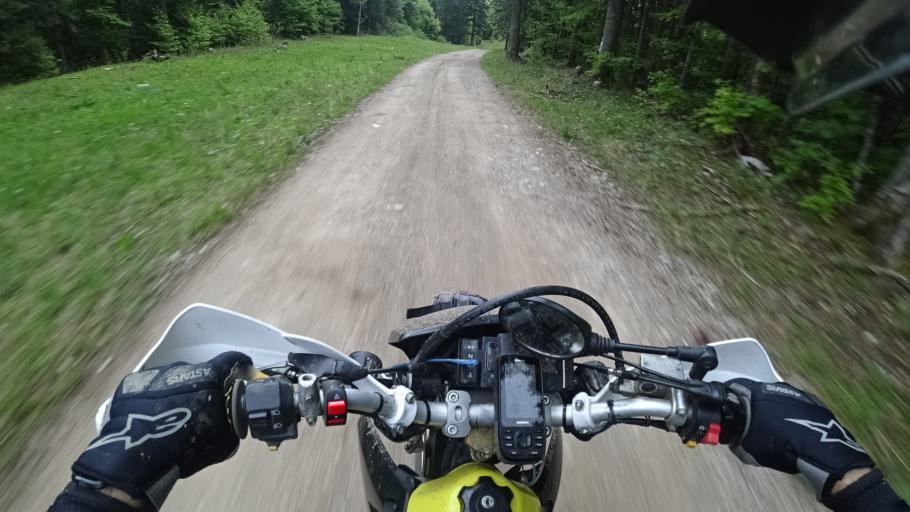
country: HR
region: Karlovacka
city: Plaski
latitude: 44.9203
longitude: 15.4279
